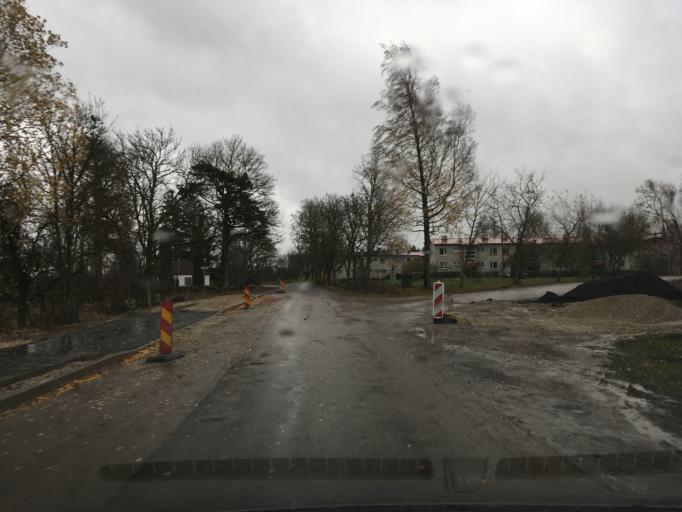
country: EE
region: Laeaene
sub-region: Lihula vald
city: Lihula
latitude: 58.6794
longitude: 23.8240
